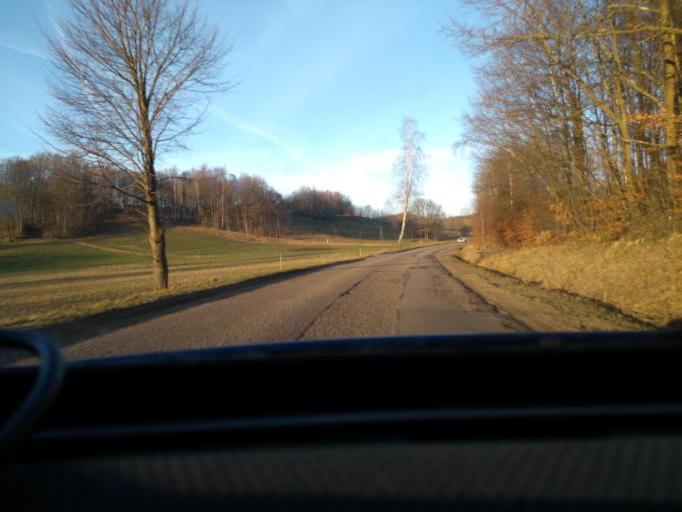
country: PL
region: Pomeranian Voivodeship
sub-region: Powiat kartuski
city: Przodkowo
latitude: 54.4081
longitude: 18.2956
